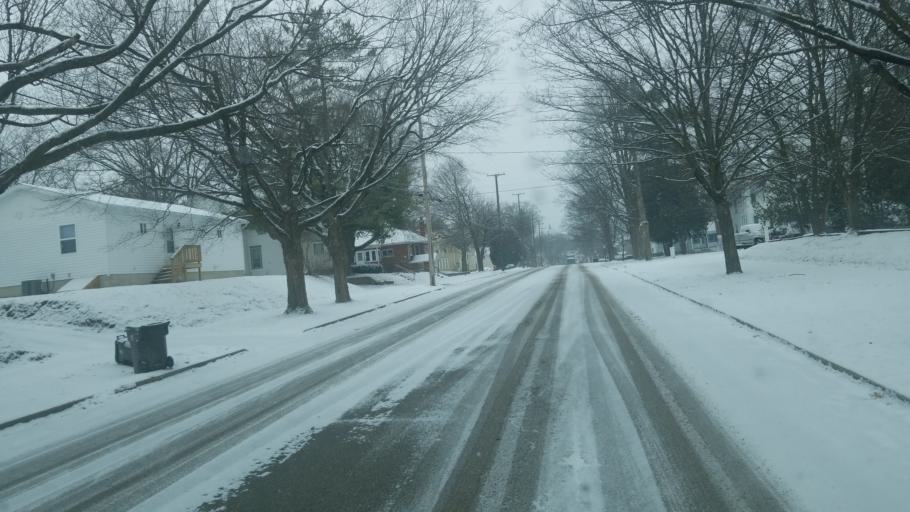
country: US
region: Michigan
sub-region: Mecosta County
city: Big Rapids
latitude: 43.6944
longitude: -85.4791
